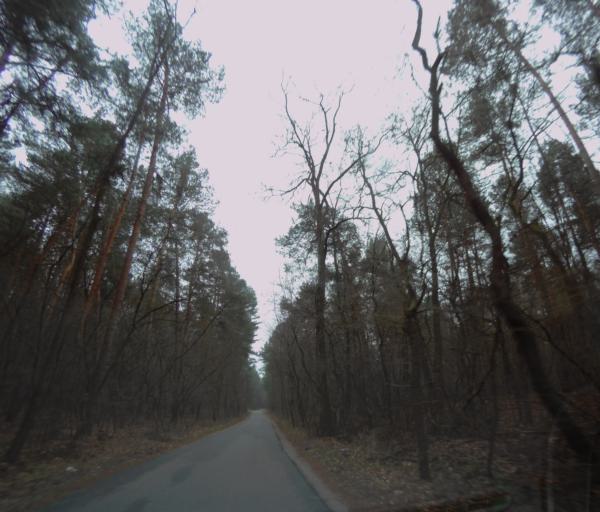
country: PL
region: Subcarpathian Voivodeship
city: Nowa Sarzyna
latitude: 50.3041
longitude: 22.3467
